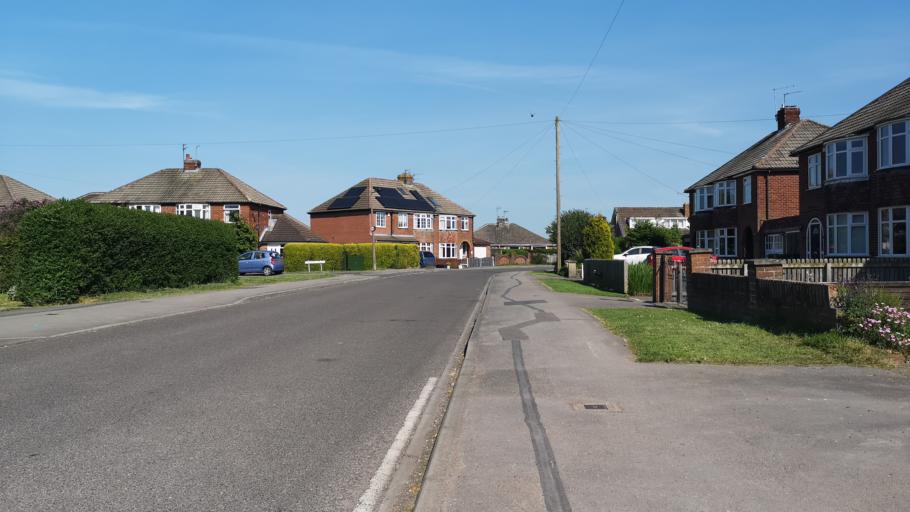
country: GB
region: England
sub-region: City of York
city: Huntington
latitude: 53.9870
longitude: -1.0654
